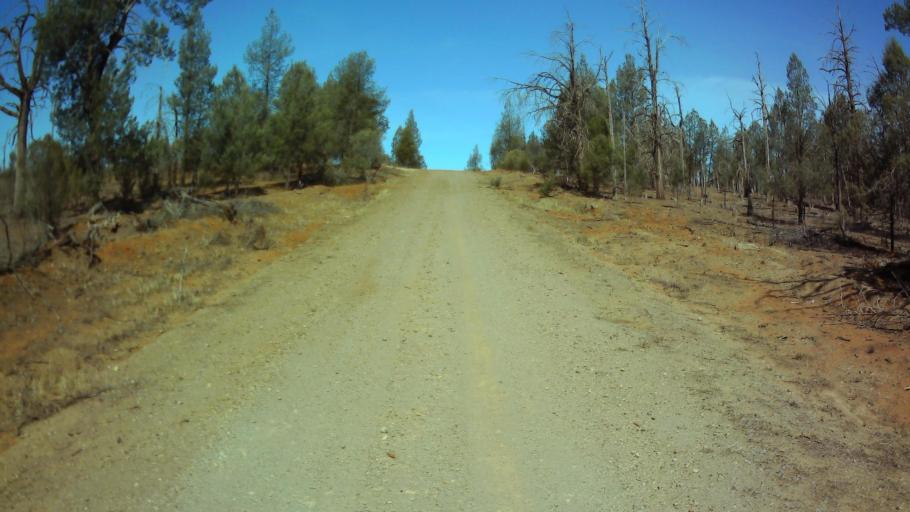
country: AU
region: New South Wales
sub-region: Weddin
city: Grenfell
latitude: -33.7819
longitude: 147.7578
